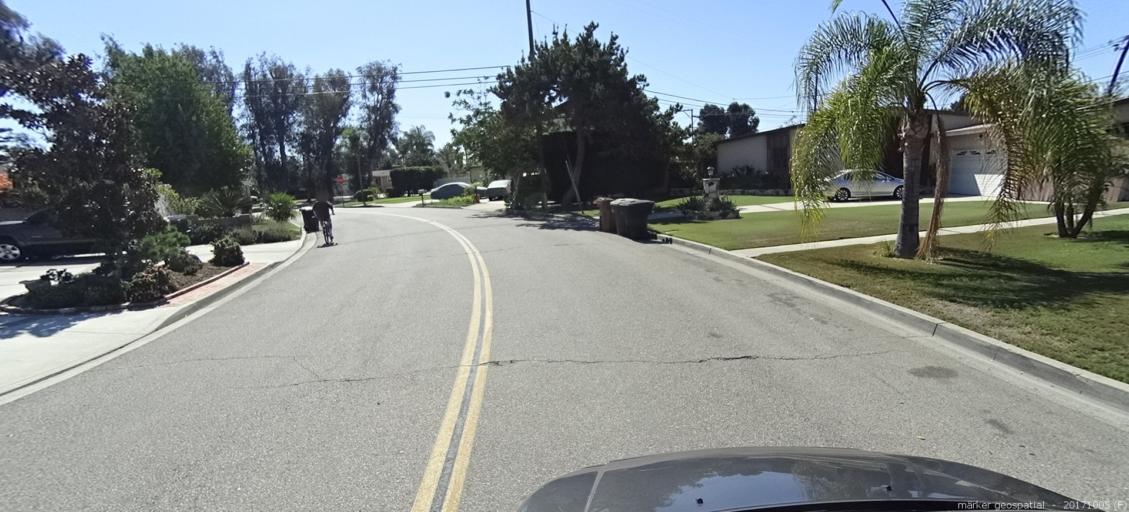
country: US
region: California
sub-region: Orange County
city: Garden Grove
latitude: 33.7819
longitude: -117.9661
